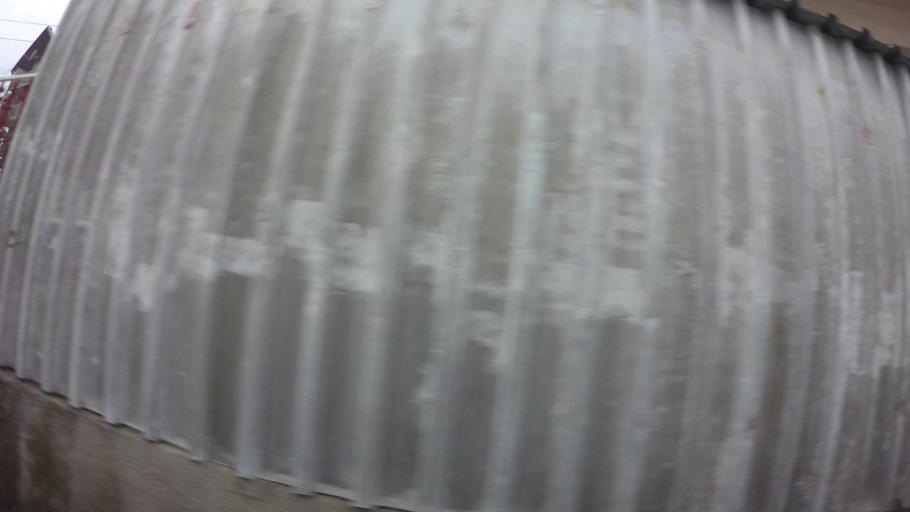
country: BA
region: Federation of Bosnia and Herzegovina
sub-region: Kanton Sarajevo
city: Sarajevo
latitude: 43.8532
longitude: 18.3594
